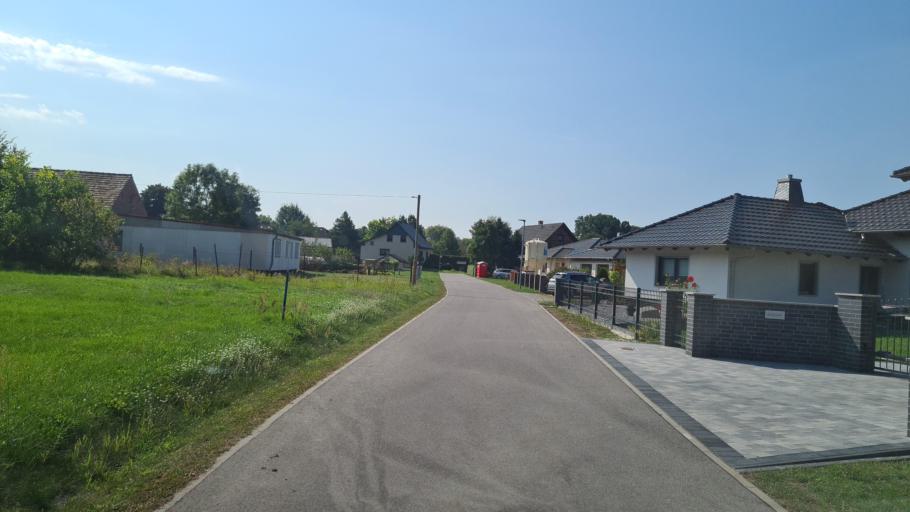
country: DE
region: Brandenburg
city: Vetschau
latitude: 51.7681
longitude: 14.1306
